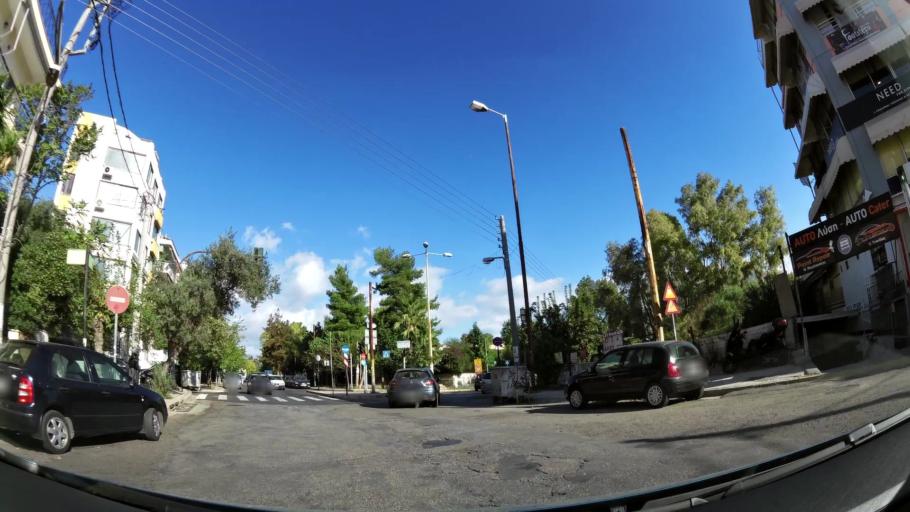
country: GR
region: Attica
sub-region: Nomarchia Athinas
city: Neo Psychiko
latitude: 37.9979
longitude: 23.7783
